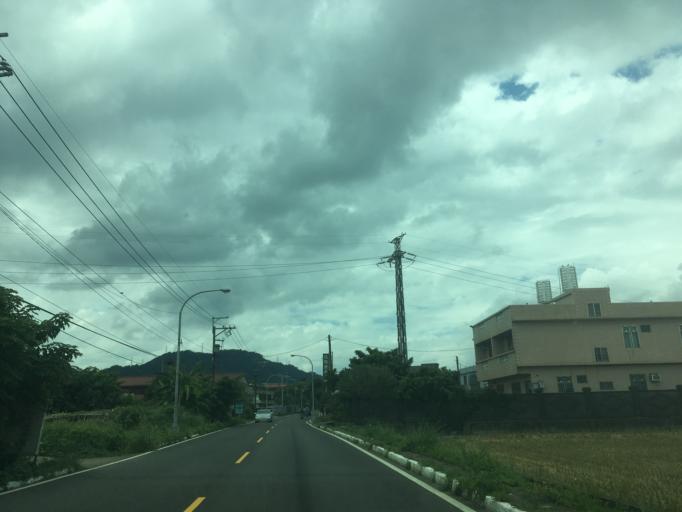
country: TW
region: Taiwan
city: Daxi
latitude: 24.8539
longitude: 121.2906
